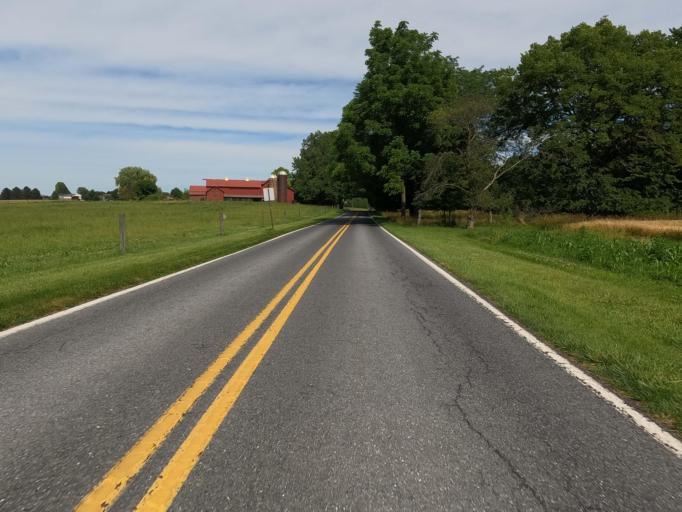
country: US
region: Pennsylvania
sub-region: Lebanon County
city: Campbelltown
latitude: 40.2700
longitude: -76.5996
